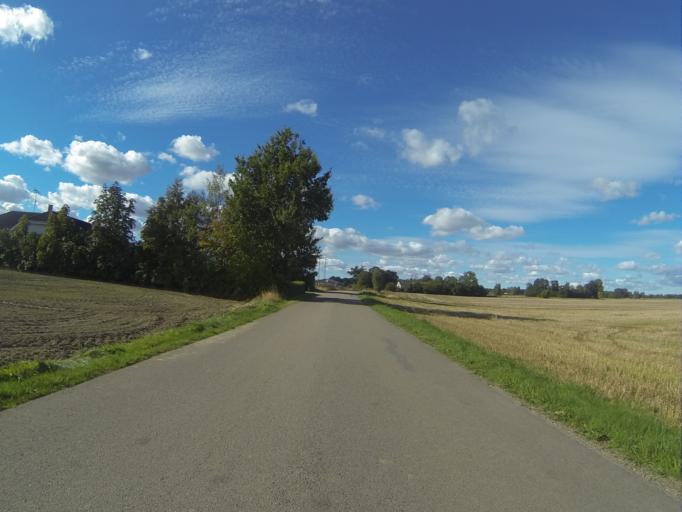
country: SE
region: Skane
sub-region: Lunds Kommun
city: Genarp
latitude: 55.7189
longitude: 13.3798
